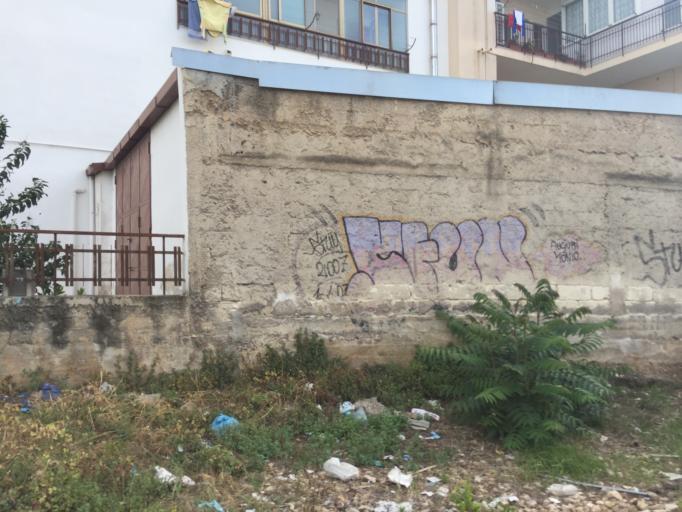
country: IT
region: Apulia
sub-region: Provincia di Bari
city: Capurso
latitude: 41.0501
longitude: 16.9220
